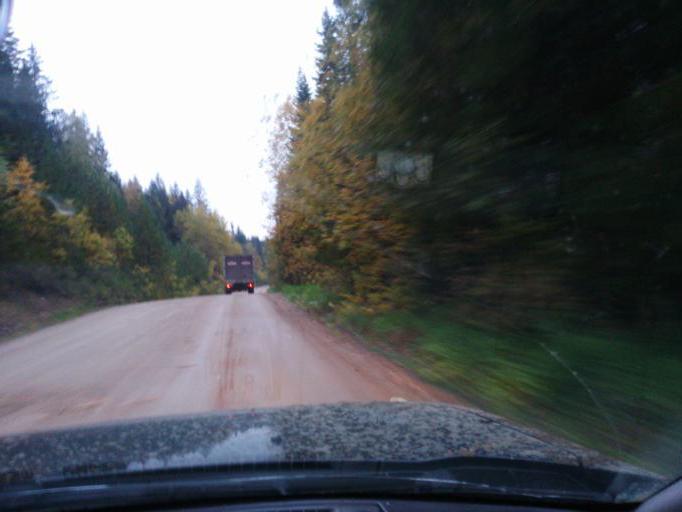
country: RU
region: Sverdlovsk
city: Sylva
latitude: 57.7987
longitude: 58.5724
